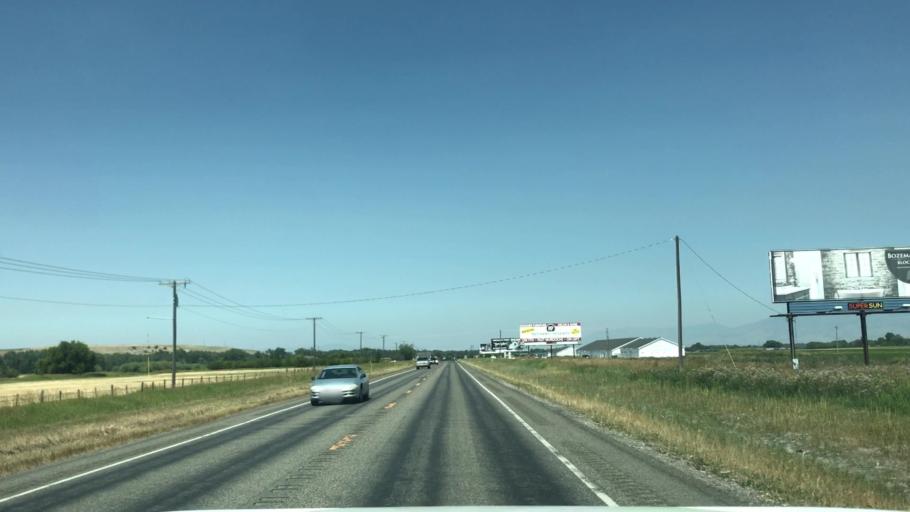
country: US
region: Montana
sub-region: Gallatin County
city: Four Corners
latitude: 45.6318
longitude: -111.1968
